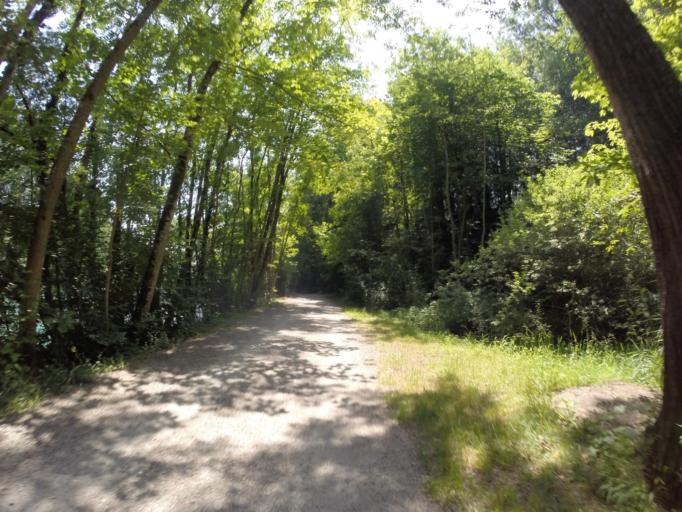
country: CH
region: Bern
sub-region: Bern-Mittelland District
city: Bern
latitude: 46.9319
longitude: 7.4616
